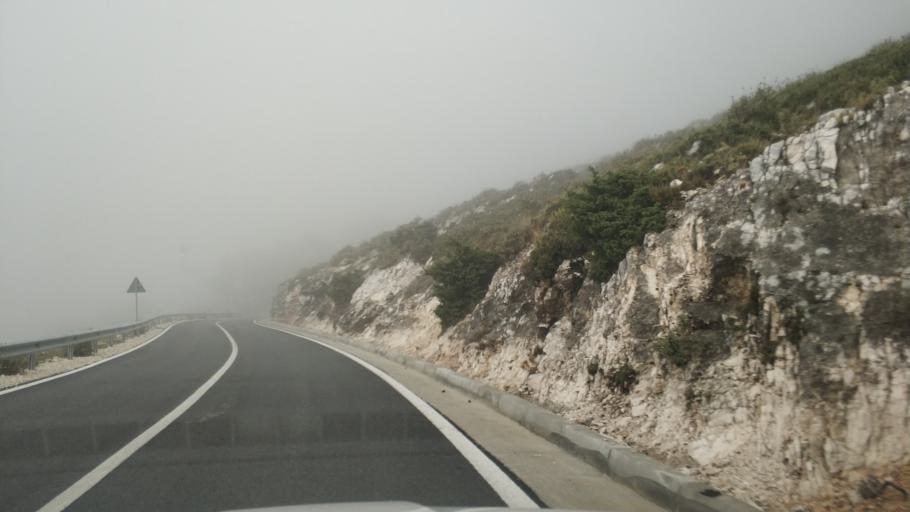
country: AL
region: Vlore
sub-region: Rrethi i Vlores
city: Vranisht
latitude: 40.1887
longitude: 19.5993
